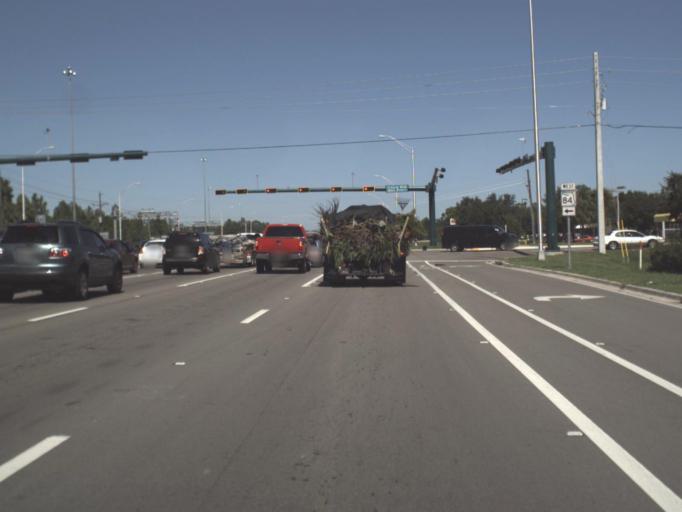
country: US
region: Florida
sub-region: Collier County
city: Golden Gate
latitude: 26.1541
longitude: -81.6863
